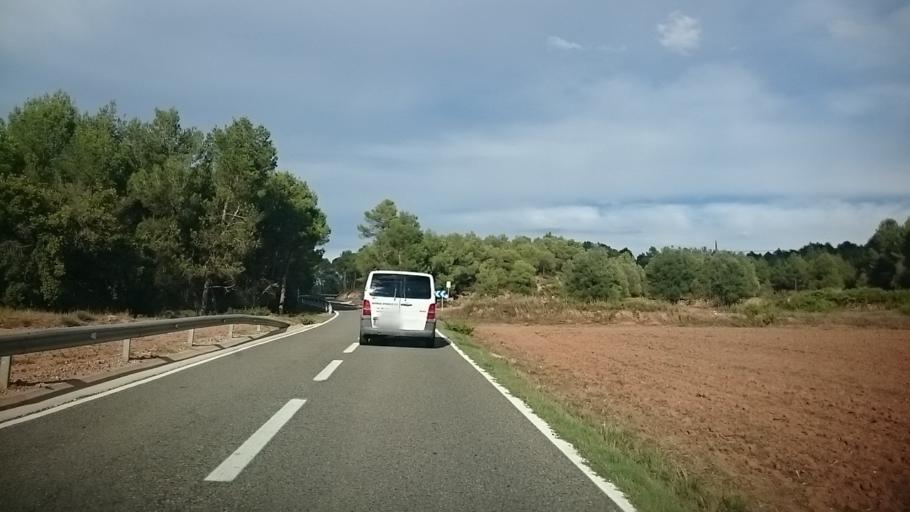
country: ES
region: Catalonia
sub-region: Provincia de Barcelona
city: Odena
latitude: 41.6244
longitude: 1.6590
